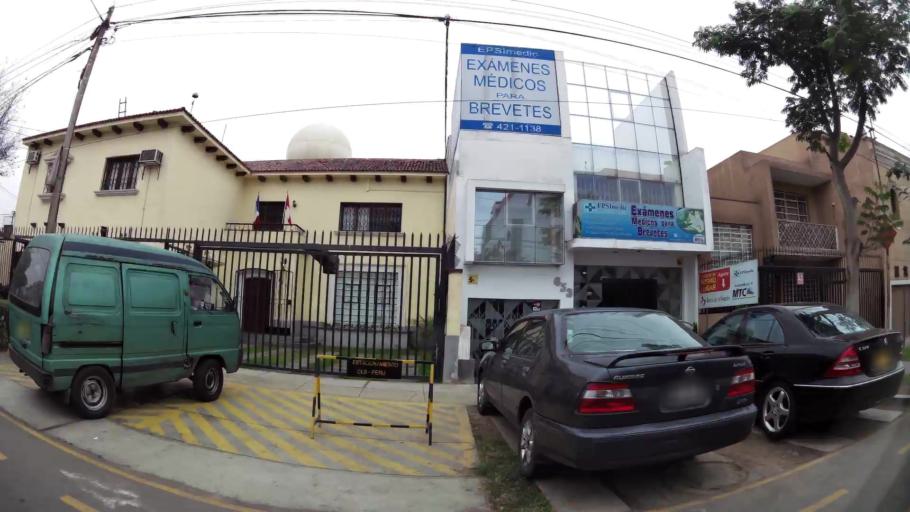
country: PE
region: Lima
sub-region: Lima
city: San Isidro
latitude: -12.0898
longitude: -77.0387
